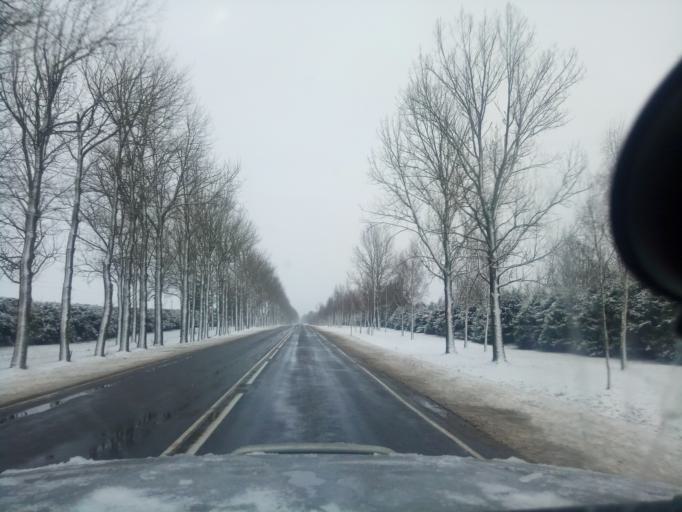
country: BY
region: Minsk
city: Haradzyeya
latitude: 53.3477
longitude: 26.5181
